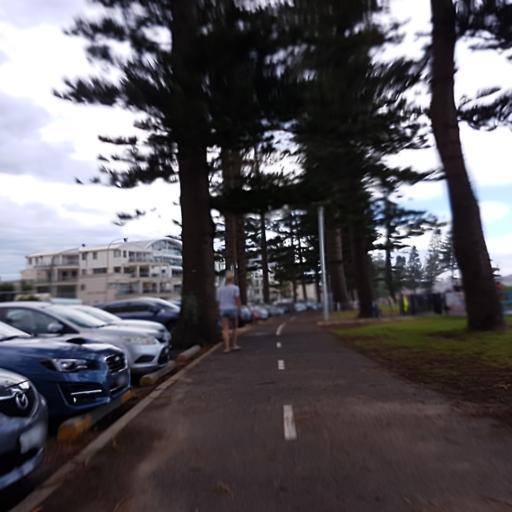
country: AU
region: New South Wales
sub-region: Manly Vale
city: Manly
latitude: -33.7942
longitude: 151.2871
